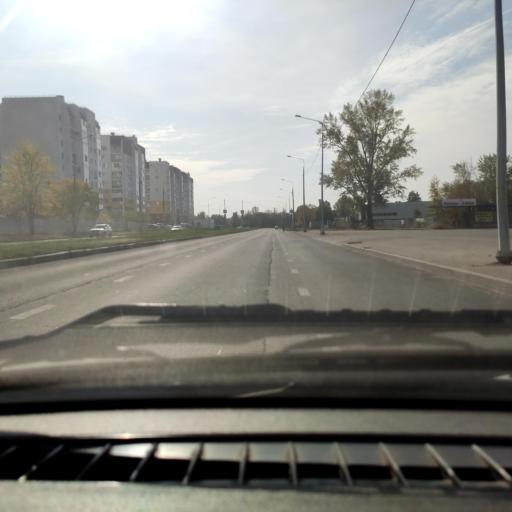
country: RU
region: Samara
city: Tol'yatti
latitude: 53.5036
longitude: 49.2698
